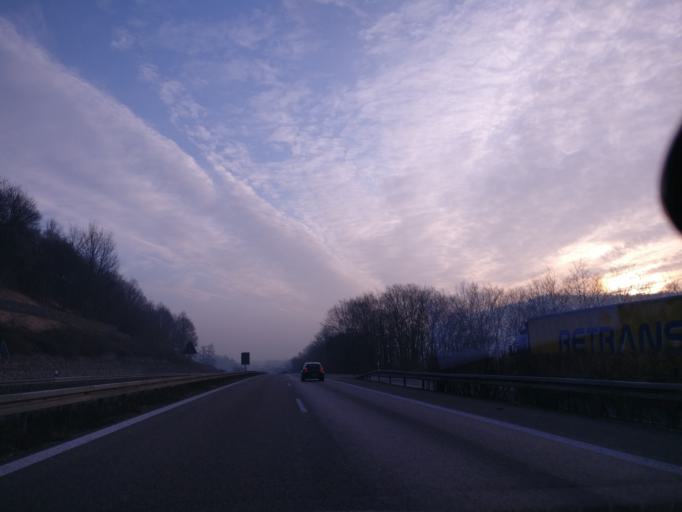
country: DE
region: Baden-Wuerttemberg
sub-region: Regierungsbezirk Stuttgart
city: Bortlingen
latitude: 48.7894
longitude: 9.6358
